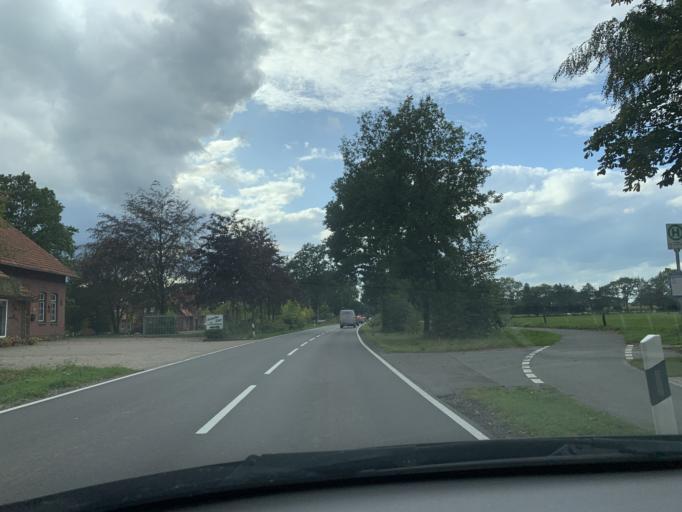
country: DE
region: Lower Saxony
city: Wiefelstede
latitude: 53.2858
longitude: 8.0239
